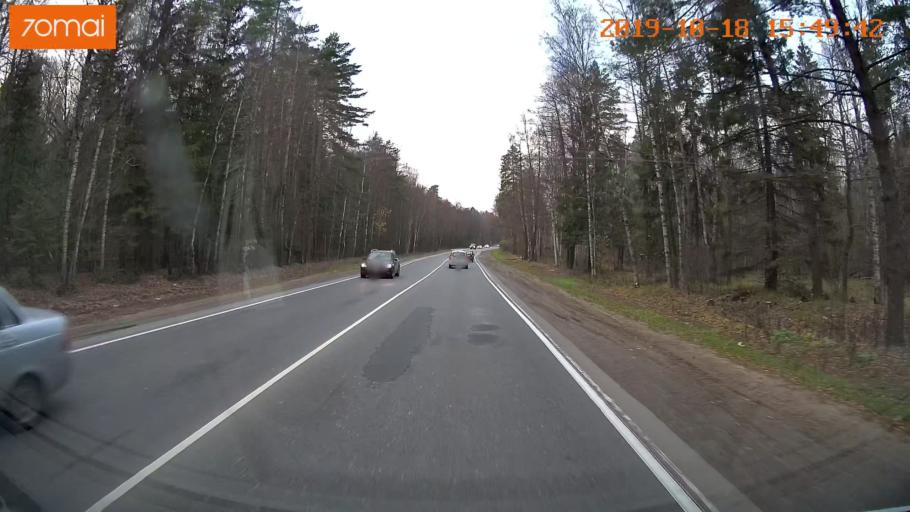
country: RU
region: Vladimir
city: Kommunar
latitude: 56.0264
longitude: 40.5712
